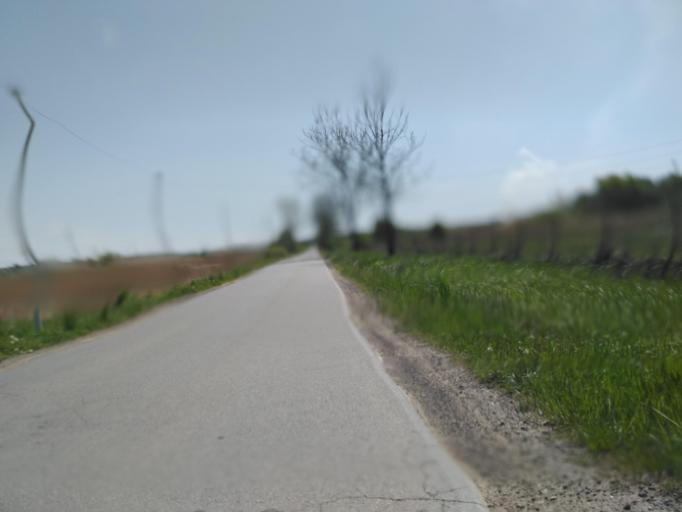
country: PL
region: Subcarpathian Voivodeship
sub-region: Powiat krosnienski
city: Miejsce Piastowe
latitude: 49.6083
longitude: 21.7739
